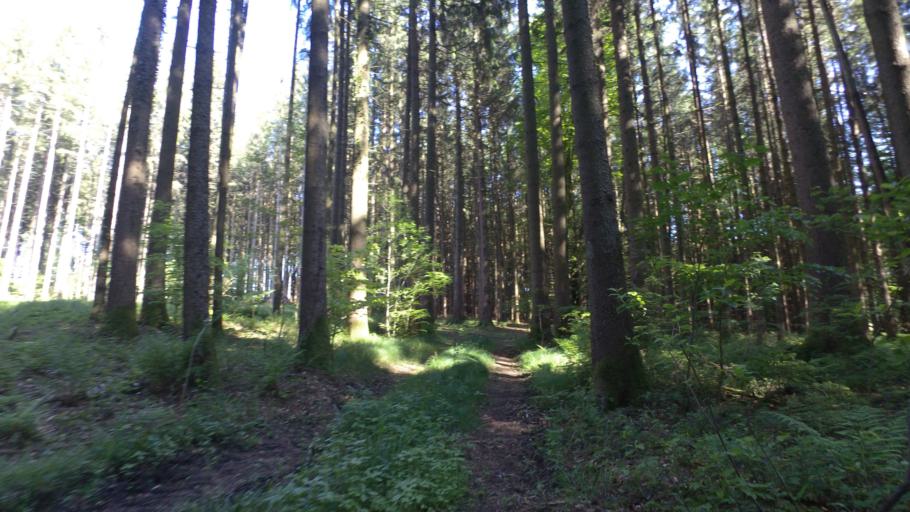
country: DE
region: Bavaria
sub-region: Upper Bavaria
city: Seeon-Seebruck
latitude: 47.9307
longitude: 12.4987
